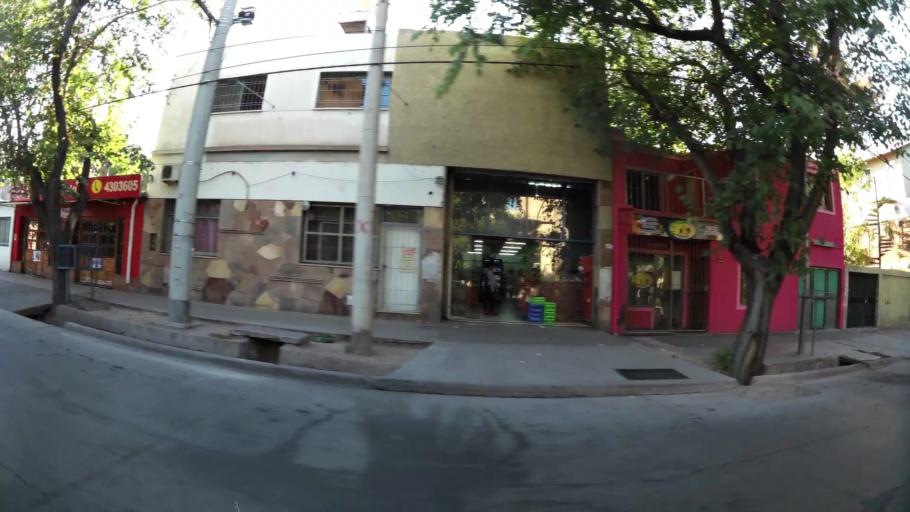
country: AR
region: Mendoza
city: Mendoza
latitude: -32.8724
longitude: -68.8397
